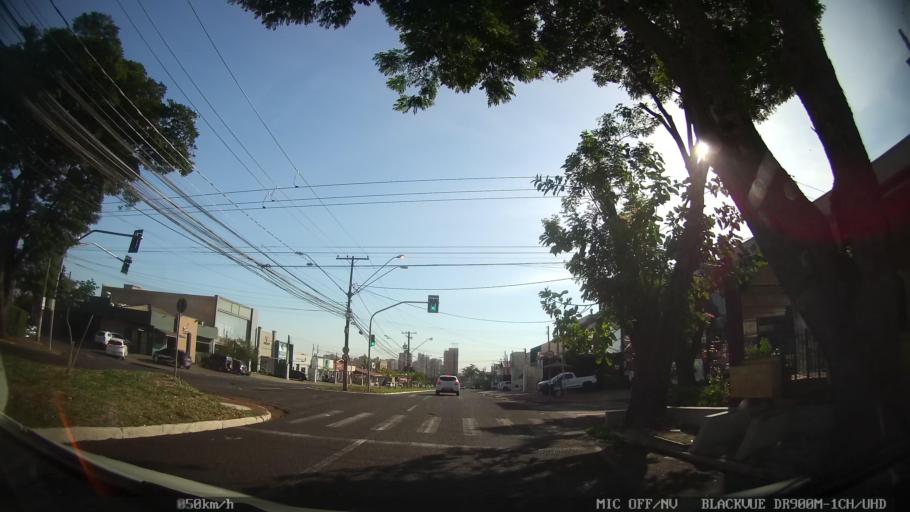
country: BR
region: Sao Paulo
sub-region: Ribeirao Preto
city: Ribeirao Preto
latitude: -21.1941
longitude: -47.8072
